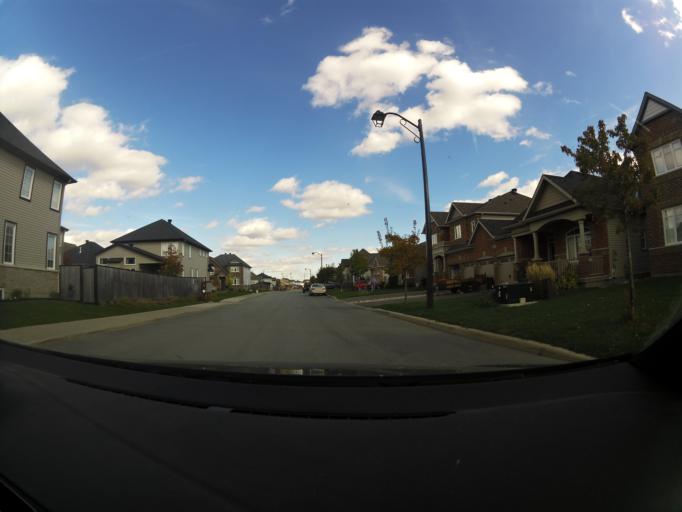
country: CA
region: Ontario
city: Bells Corners
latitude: 45.2746
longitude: -75.8875
